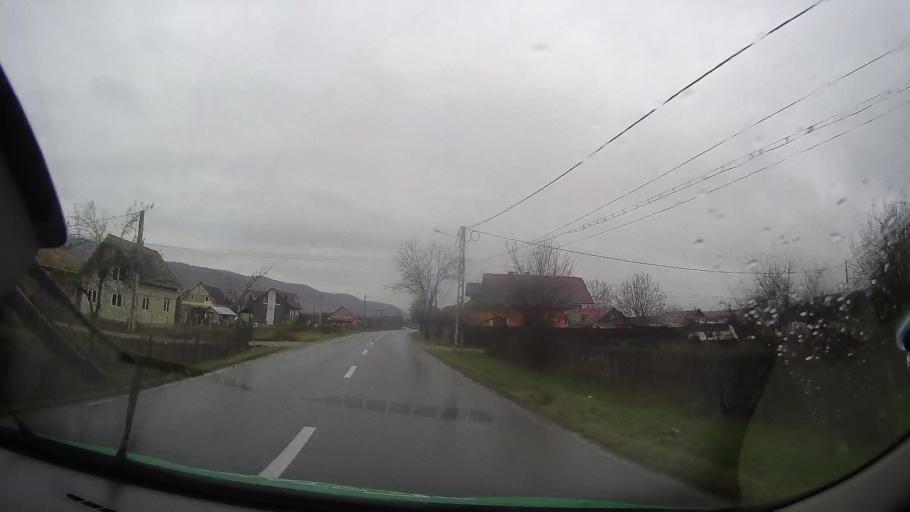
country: RO
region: Bistrita-Nasaud
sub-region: Comuna Mariselu
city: Mariselu
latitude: 47.0310
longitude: 24.4858
